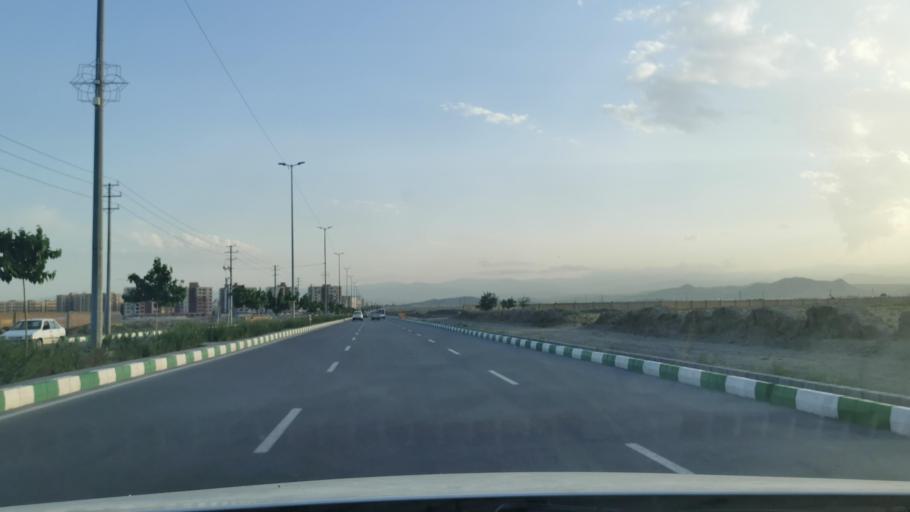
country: IR
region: Razavi Khorasan
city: Mashhad
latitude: 36.3991
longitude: 59.4776
